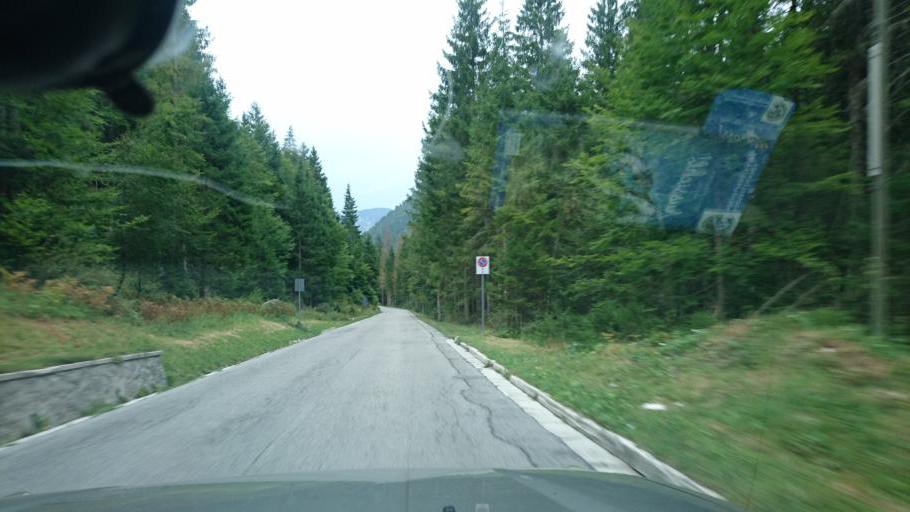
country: IT
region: Friuli Venezia Giulia
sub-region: Provincia di Udine
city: Malborghetto
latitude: 46.4684
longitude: 13.4908
